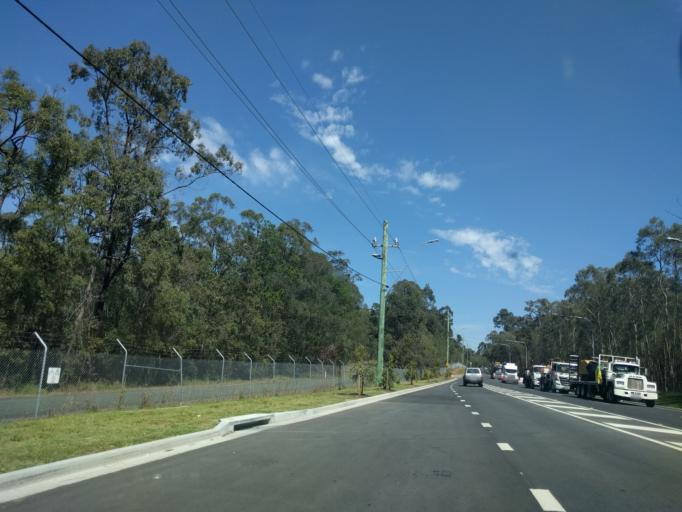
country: AU
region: Queensland
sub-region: Brisbane
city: Forest Lake
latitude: -27.6482
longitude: 152.9827
